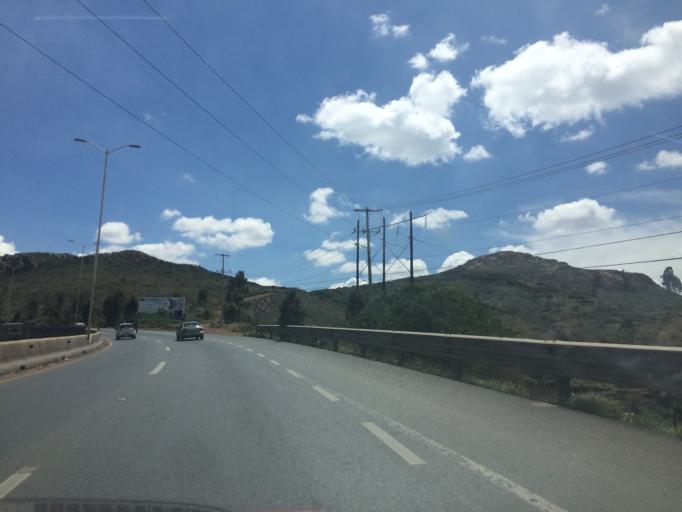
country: MX
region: Zacatecas
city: Zacatecas
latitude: 22.7539
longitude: -102.5788
